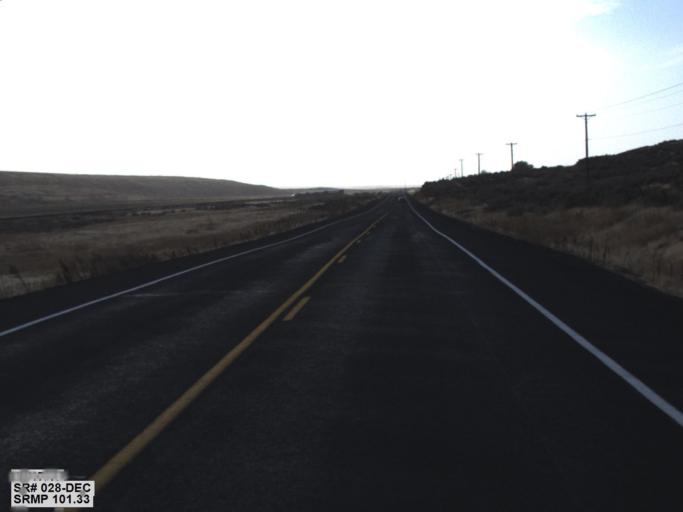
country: US
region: Washington
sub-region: Adams County
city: Ritzville
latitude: 47.3518
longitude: -118.5395
